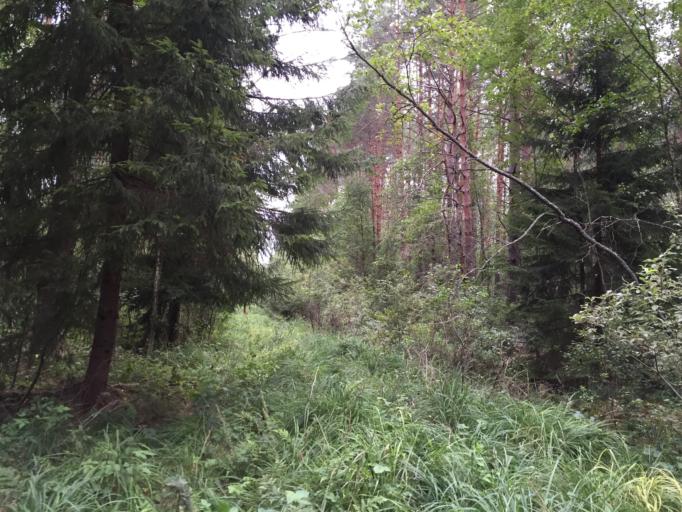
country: LV
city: Tireli
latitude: 56.8492
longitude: 23.6732
